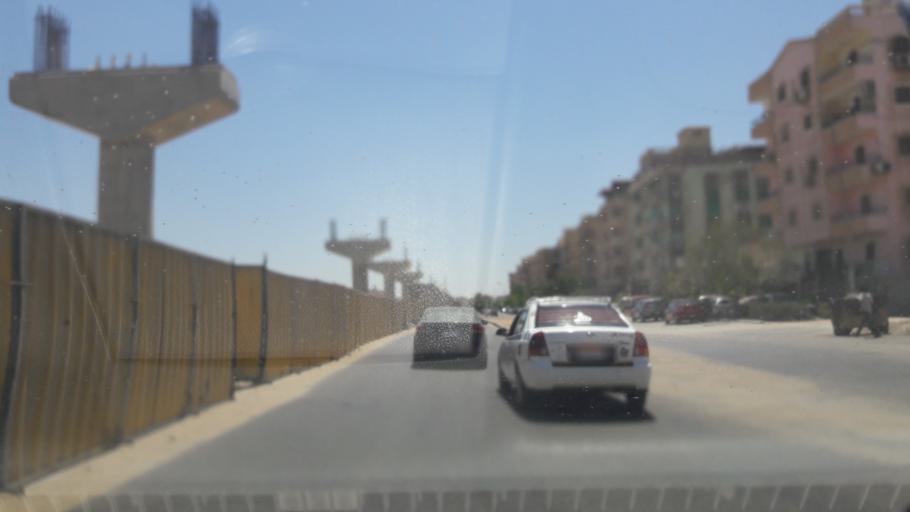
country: EG
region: Al Jizah
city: Madinat Sittah Uktubar
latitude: 29.9723
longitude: 30.9378
